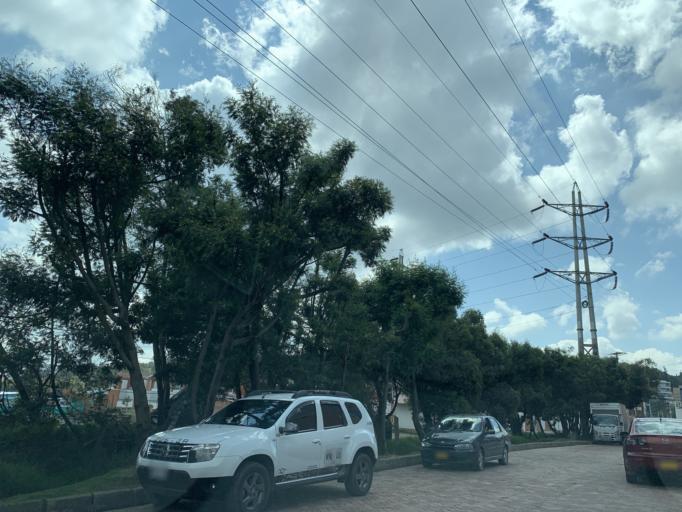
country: CO
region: Boyaca
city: Tunja
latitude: 5.5552
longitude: -73.3463
